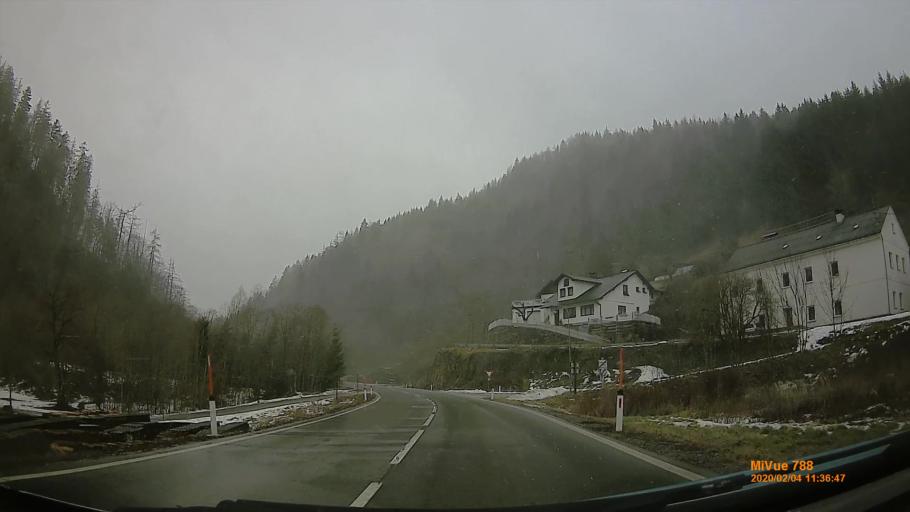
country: AT
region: Styria
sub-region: Politischer Bezirk Bruck-Muerzzuschlag
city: Neuberg an der Muerz
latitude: 47.6746
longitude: 15.5457
